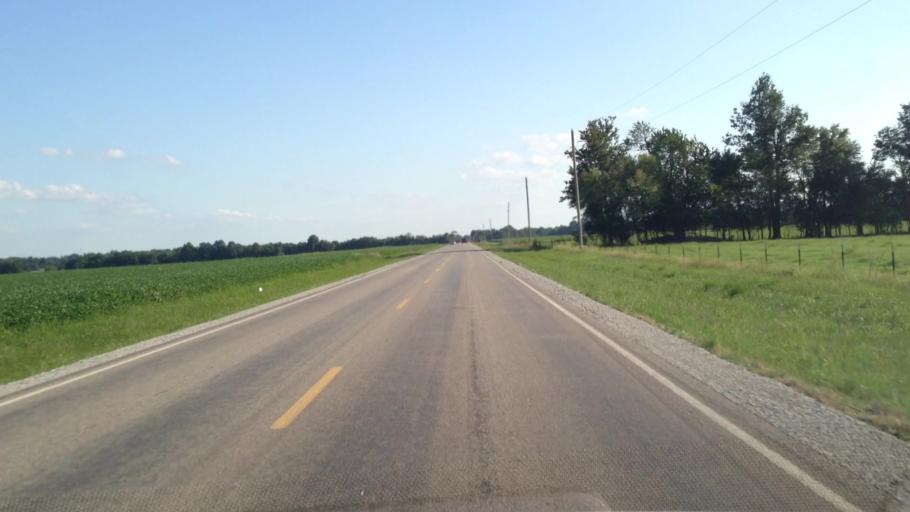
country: US
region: Kansas
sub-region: Crawford County
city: Pittsburg
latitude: 37.3615
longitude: -94.6315
